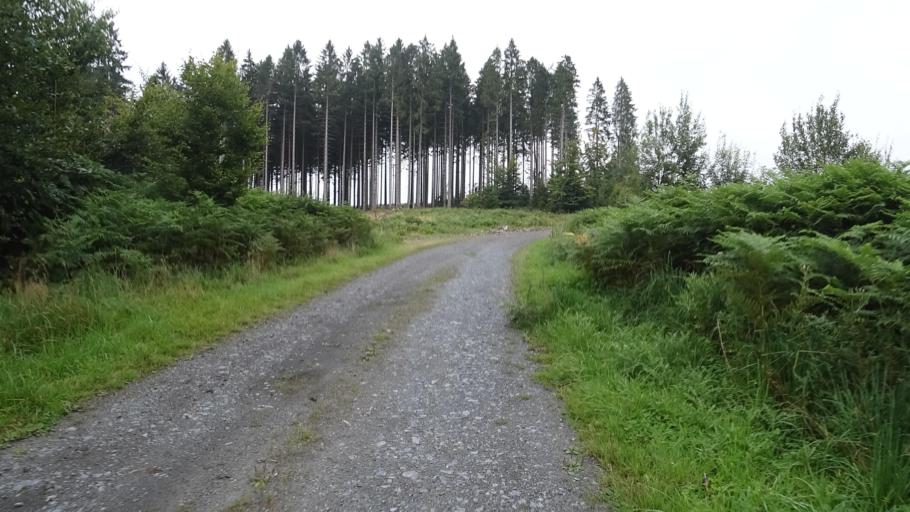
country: BE
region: Wallonia
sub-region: Province du Luxembourg
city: Chiny
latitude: 49.7900
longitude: 5.3250
